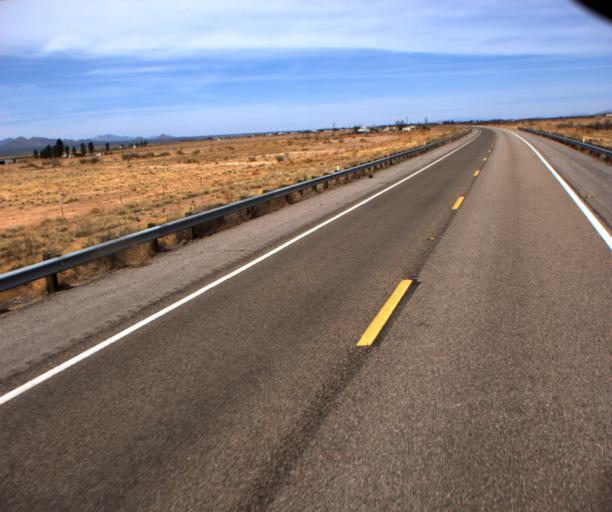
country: US
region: Arizona
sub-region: Cochise County
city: Pirtleville
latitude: 31.6454
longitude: -109.6727
